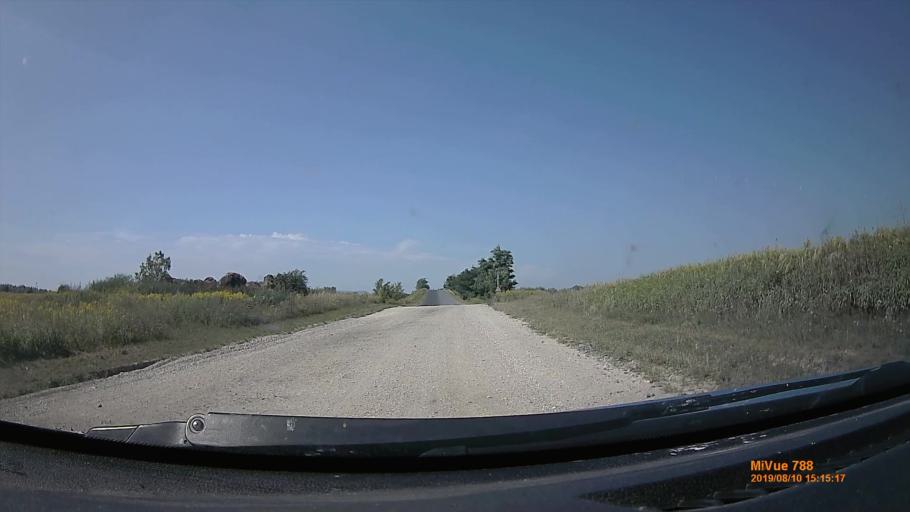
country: HU
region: Somogy
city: Fonyod
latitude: 46.6983
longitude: 17.5576
